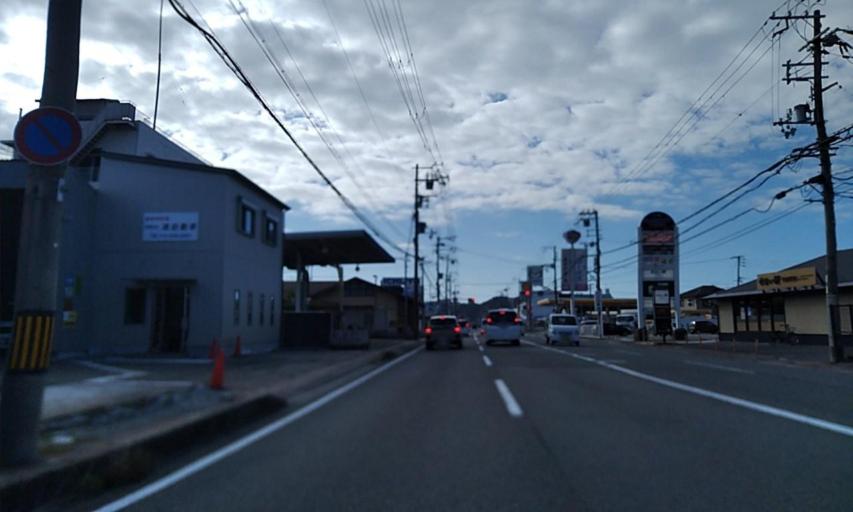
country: JP
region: Wakayama
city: Minato
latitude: 34.2133
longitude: 135.1595
